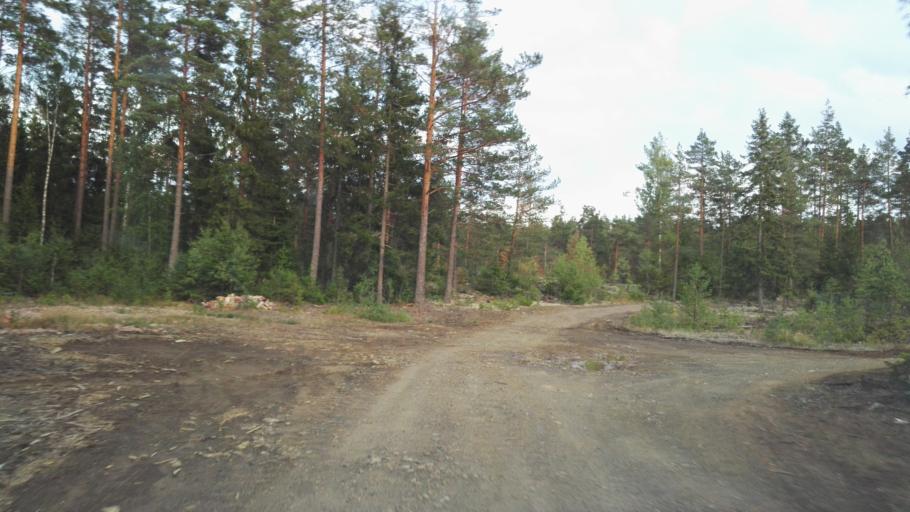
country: SE
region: Joenkoeping
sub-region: Vetlanda Kommun
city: Landsbro
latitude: 57.2945
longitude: 14.8487
